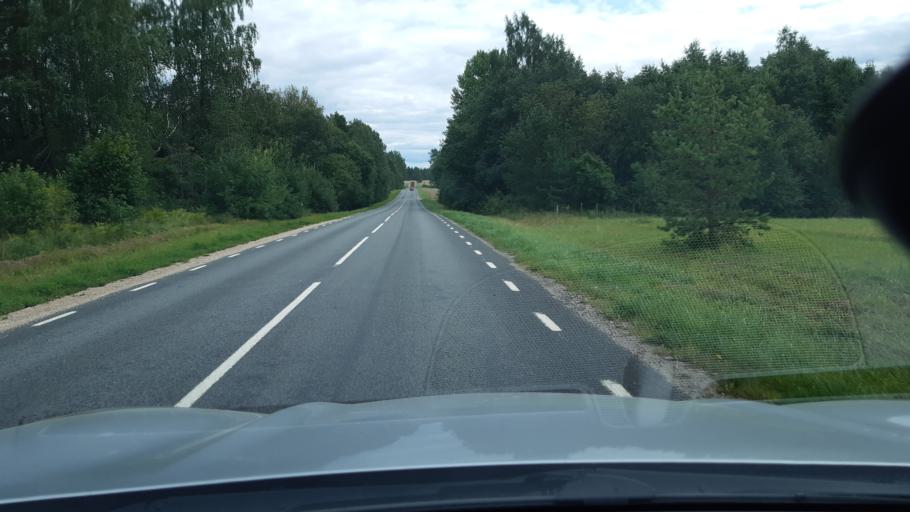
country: EE
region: Raplamaa
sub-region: Maerjamaa vald
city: Marjamaa
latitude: 59.0438
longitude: 24.4838
